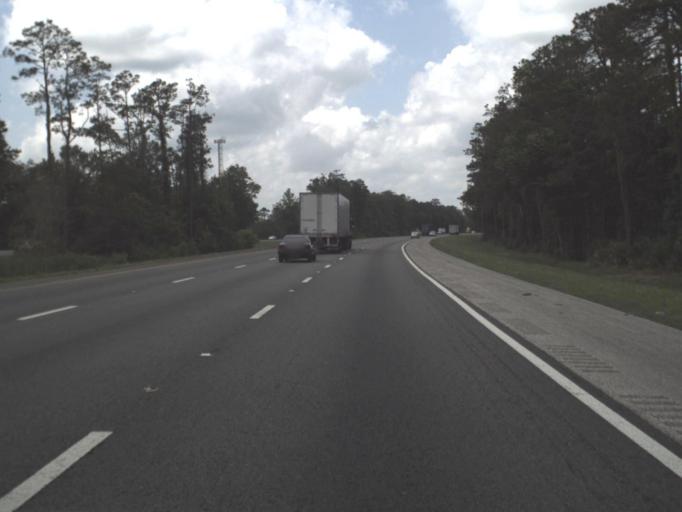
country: US
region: Florida
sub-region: Saint Johns County
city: Butler Beach
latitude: 29.6797
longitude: -81.3167
